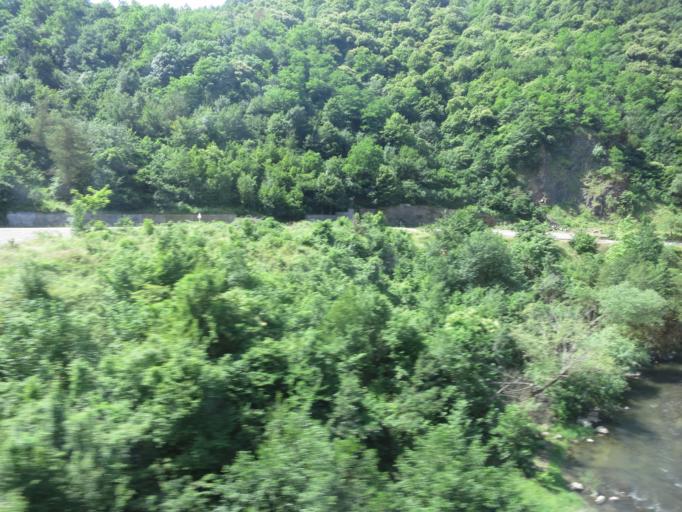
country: GE
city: Shorapani
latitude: 42.0944
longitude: 43.1260
